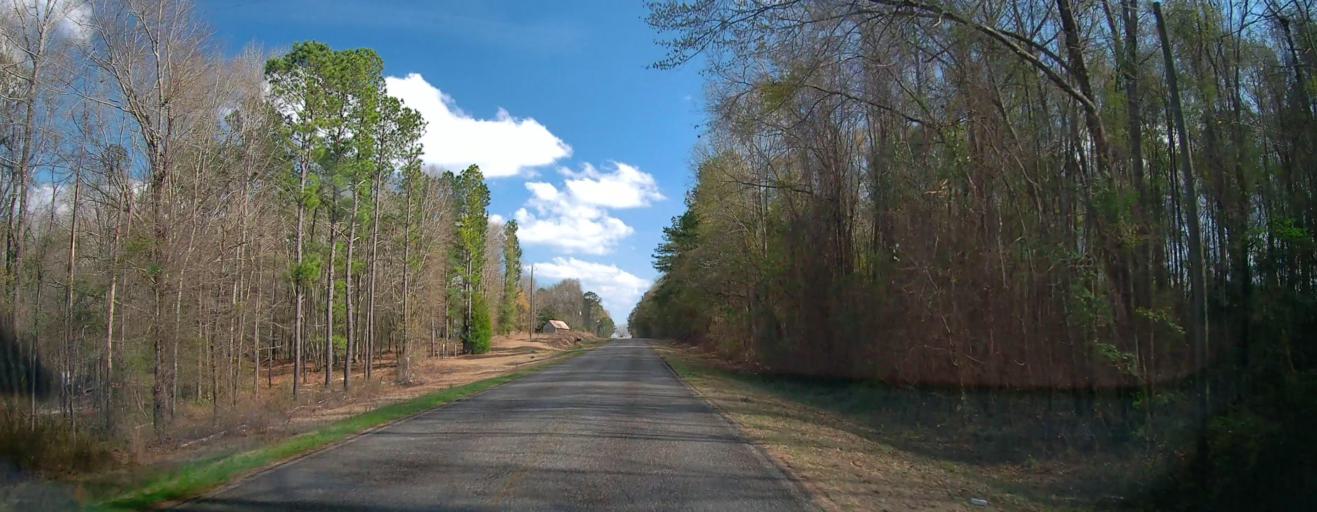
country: US
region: Georgia
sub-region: Twiggs County
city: Jeffersonville
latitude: 32.6603
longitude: -83.2247
